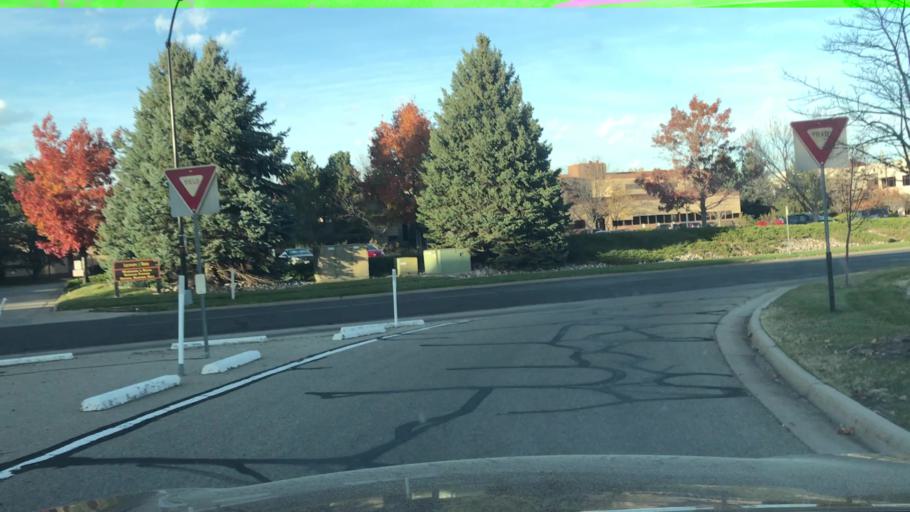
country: US
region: Colorado
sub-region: Boulder County
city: Gunbarrel
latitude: 40.0640
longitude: -105.2126
